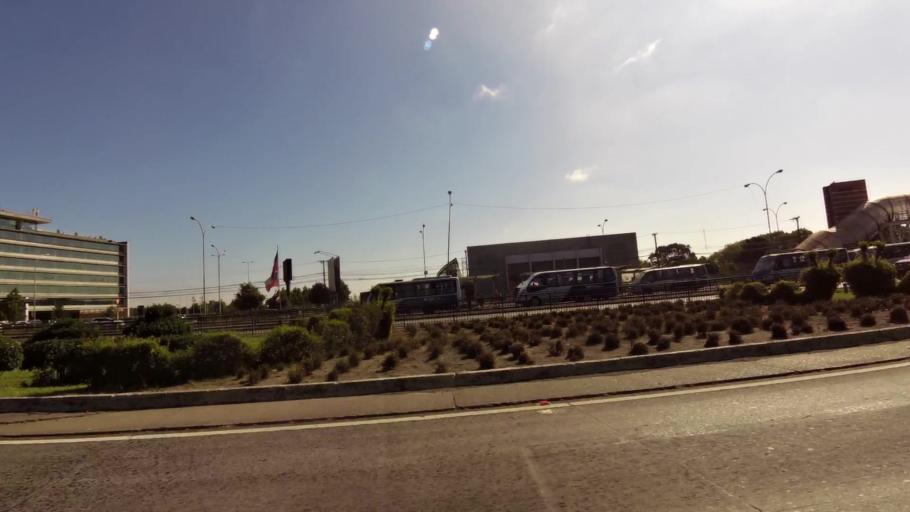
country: CL
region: Biobio
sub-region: Provincia de Concepcion
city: Concepcion
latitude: -36.7917
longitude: -73.0701
